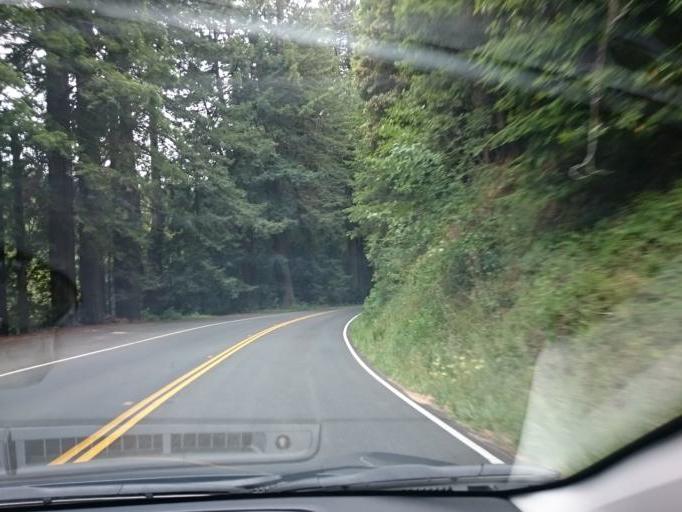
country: US
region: California
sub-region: Mendocino County
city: Fort Bragg
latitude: 39.1793
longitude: -123.7018
